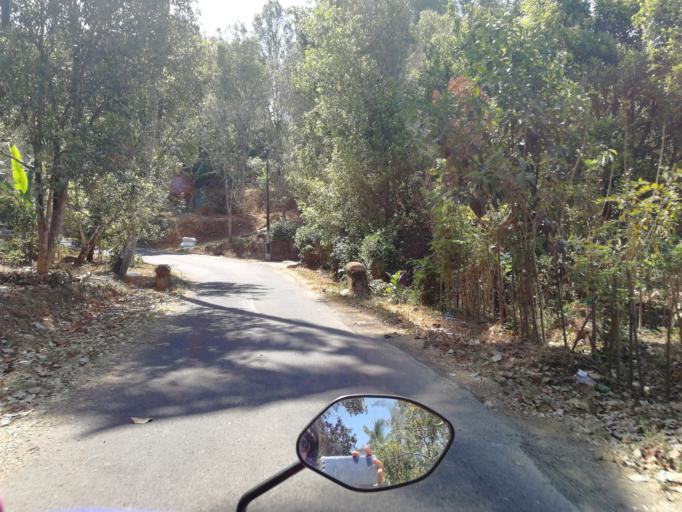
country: ID
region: Bali
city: Banjar Kedisan
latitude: -8.1552
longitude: 115.3069
